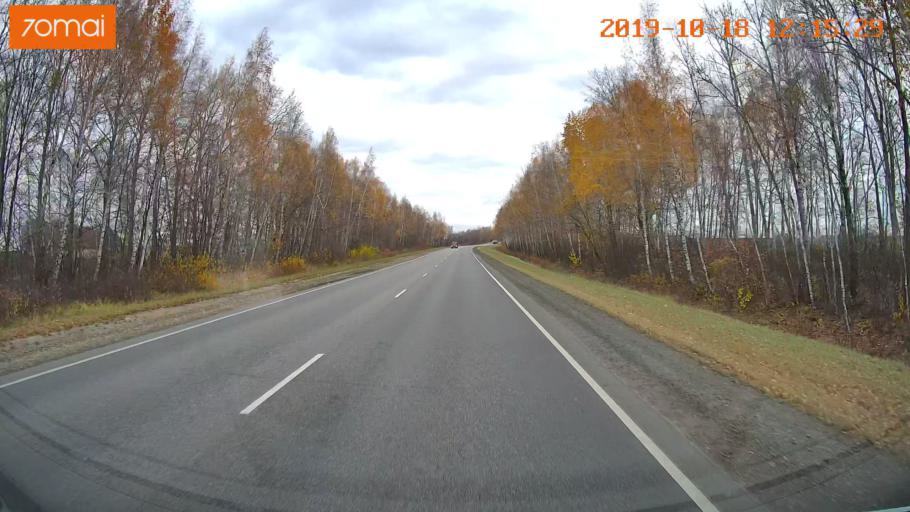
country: RU
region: Rjazan
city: Zakharovo
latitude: 54.4438
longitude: 39.4002
